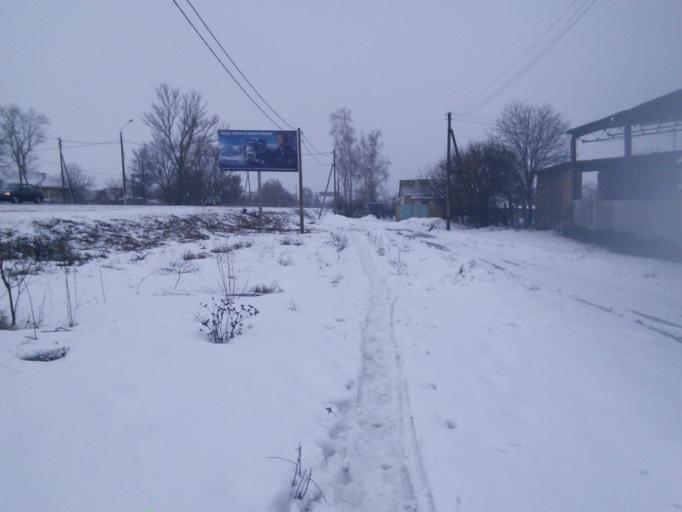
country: RU
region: Kursk
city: Chernitsyno
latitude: 51.5768
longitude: 36.0799
